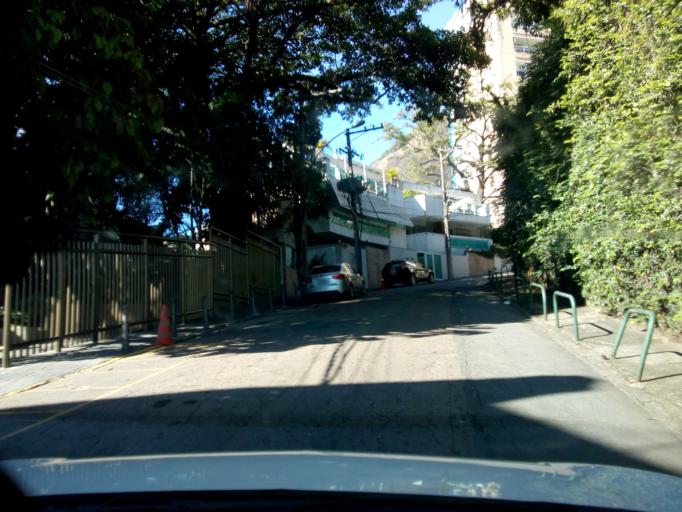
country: BR
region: Rio de Janeiro
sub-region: Rio De Janeiro
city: Rio de Janeiro
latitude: -22.9855
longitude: -43.2318
